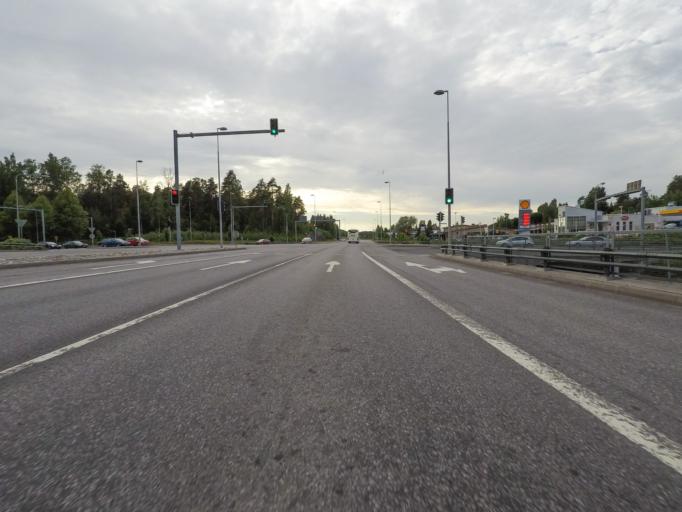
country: FI
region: Southern Savonia
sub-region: Savonlinna
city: Savonlinna
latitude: 61.8680
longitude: 28.9262
